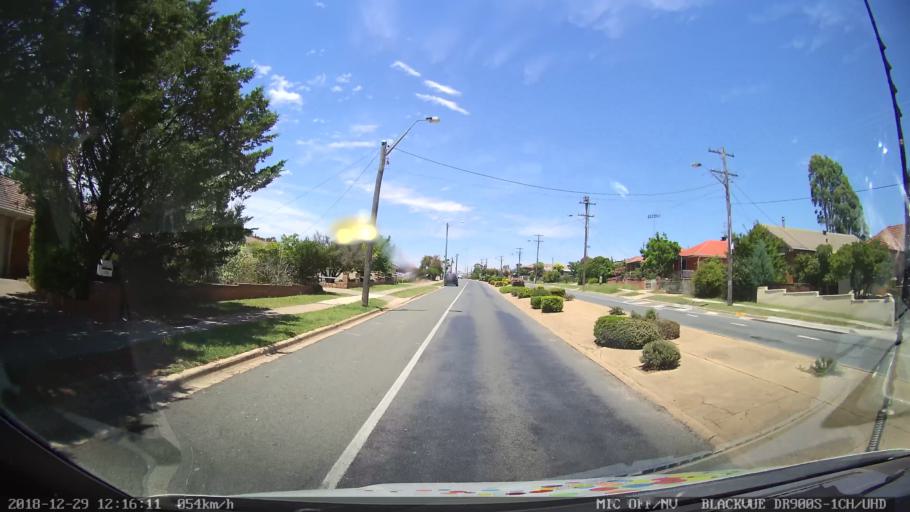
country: AU
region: New South Wales
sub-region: Queanbeyan
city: Queanbeyan
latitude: -35.3675
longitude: 149.2333
